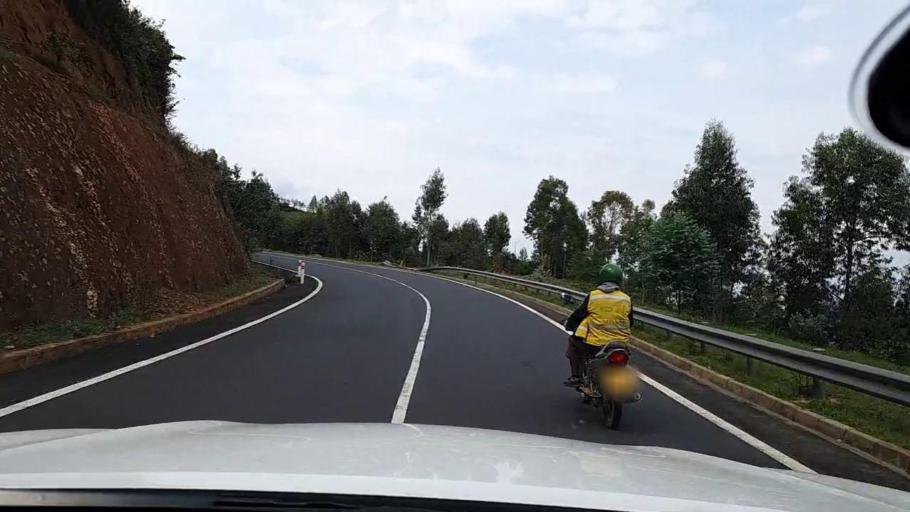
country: RW
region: Western Province
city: Kibuye
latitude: -2.1745
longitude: 29.2921
